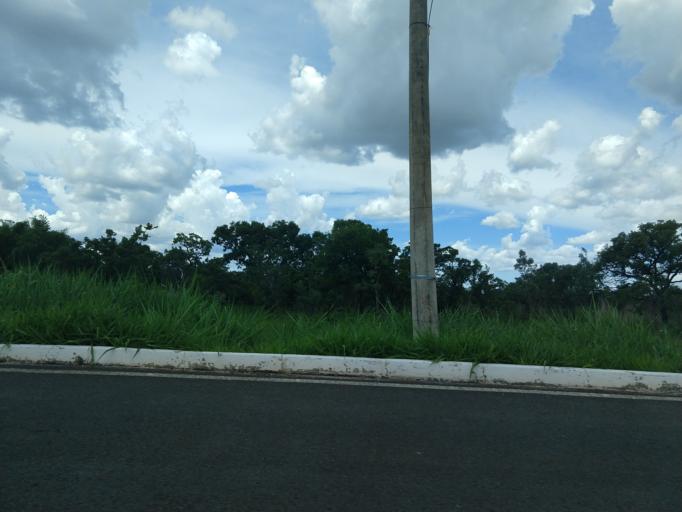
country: BR
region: Federal District
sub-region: Brasilia
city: Brasilia
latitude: -15.7508
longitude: -47.8780
